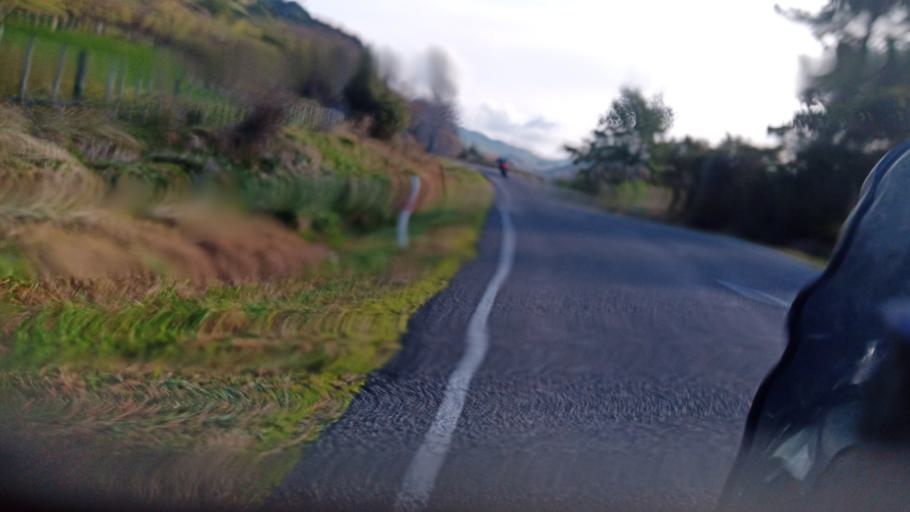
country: NZ
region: Gisborne
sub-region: Gisborne District
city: Gisborne
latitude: -38.4448
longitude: 177.6199
